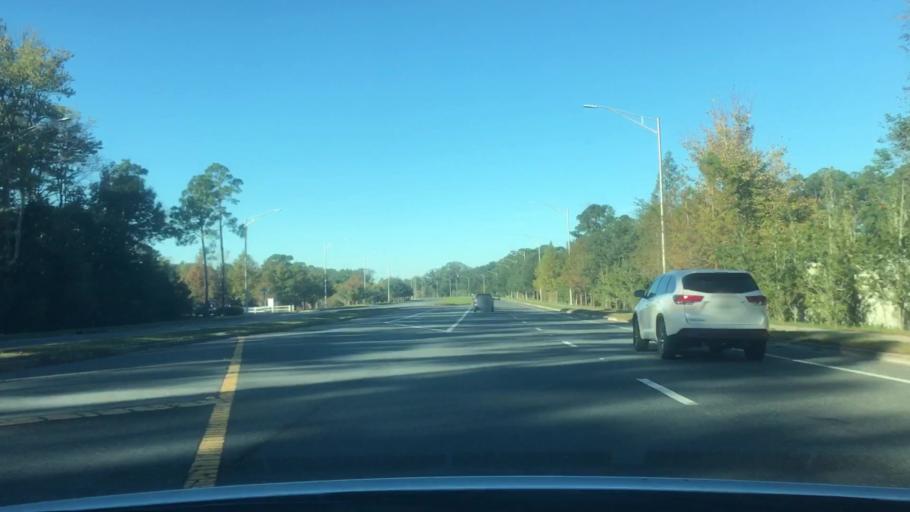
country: US
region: Florida
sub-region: Duval County
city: Jacksonville
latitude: 30.4761
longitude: -81.6200
